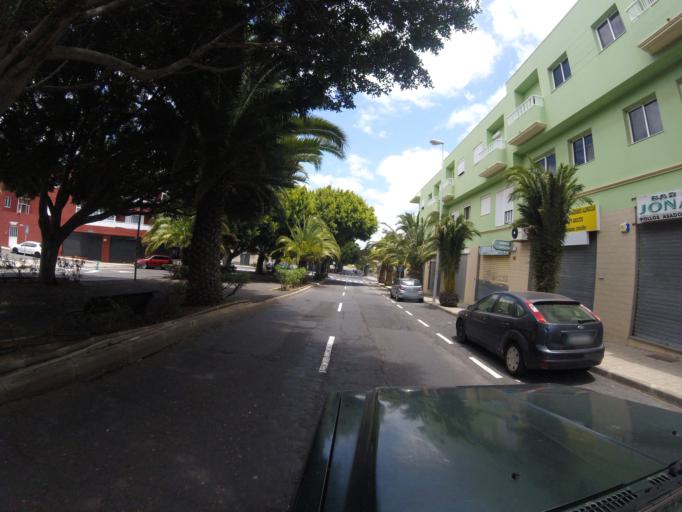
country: ES
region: Canary Islands
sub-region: Provincia de Santa Cruz de Tenerife
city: La Laguna
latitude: 28.4444
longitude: -16.3100
